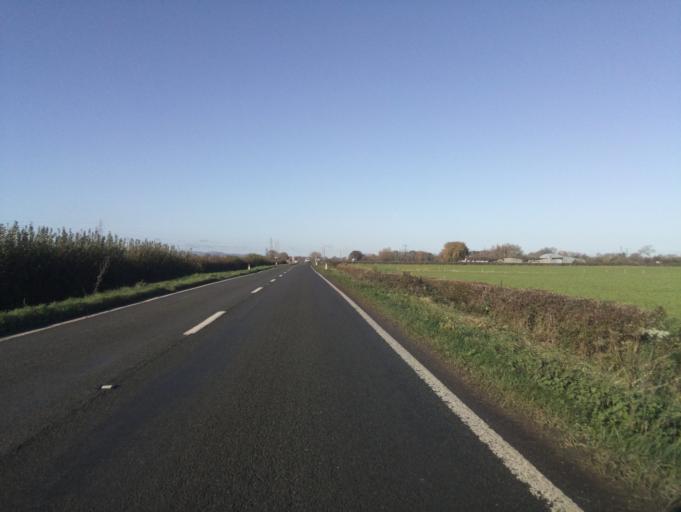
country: GB
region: England
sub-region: Somerset
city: Westonzoyland
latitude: 51.1119
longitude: -2.9557
